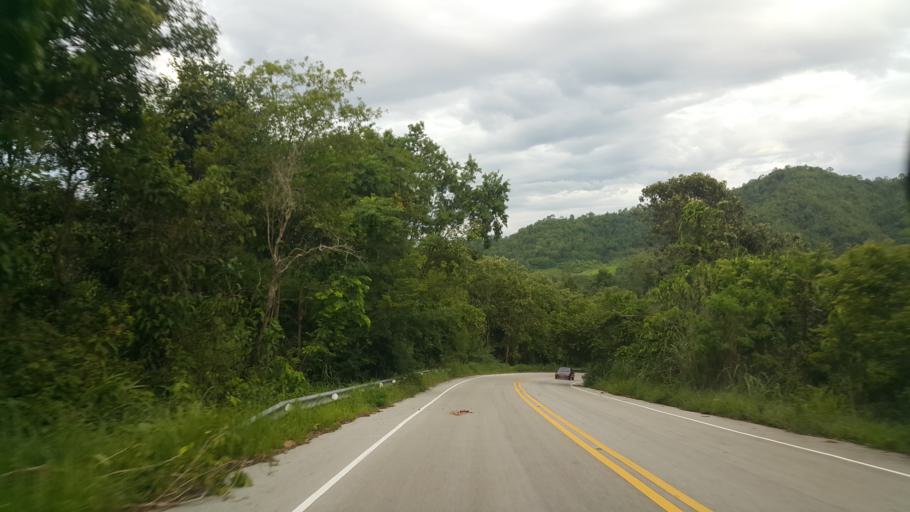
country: TH
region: Loei
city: Na Haeo
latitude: 17.5000
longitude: 101.0922
